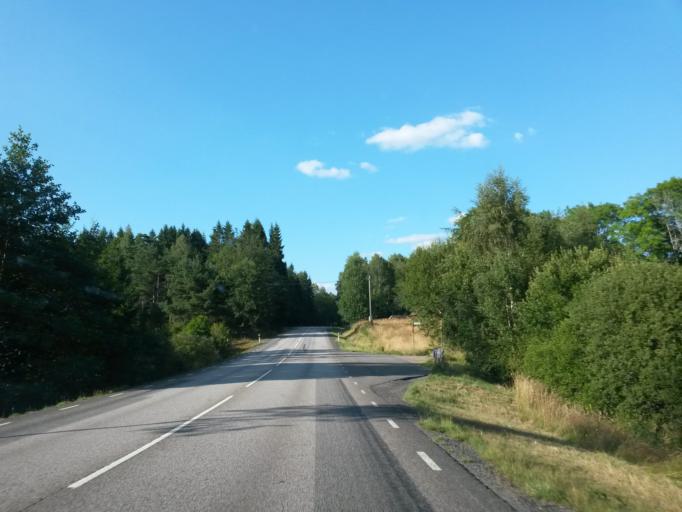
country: SE
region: Vaestra Goetaland
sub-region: Lerums Kommun
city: Grabo
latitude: 57.8975
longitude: 12.3340
